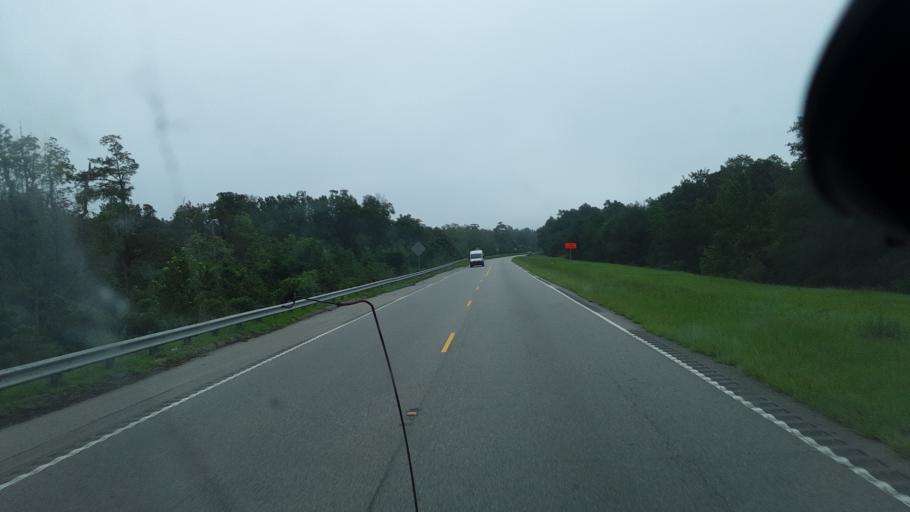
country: US
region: South Carolina
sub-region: Florence County
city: Johnsonville
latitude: 33.9103
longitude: -79.4260
